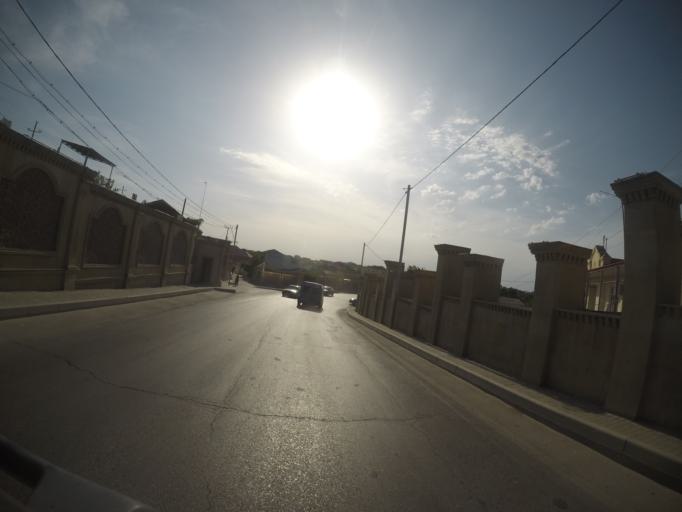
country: AZ
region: Baki
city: Binagadi
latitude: 40.4686
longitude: 49.8411
